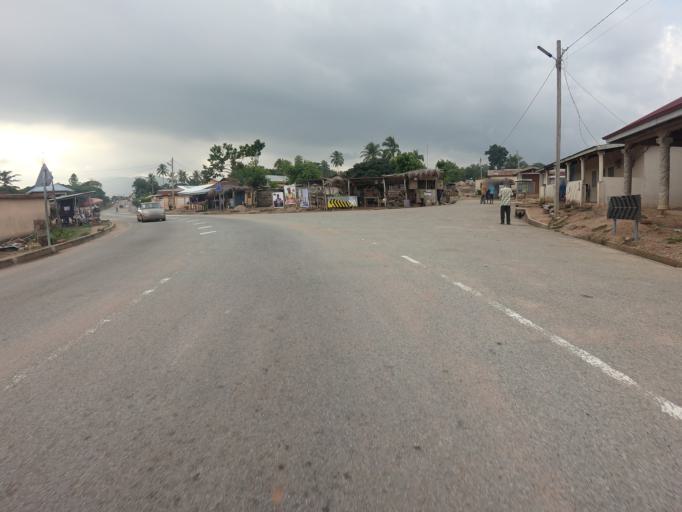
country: GH
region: Volta
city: Ho
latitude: 6.7705
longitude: 0.4810
